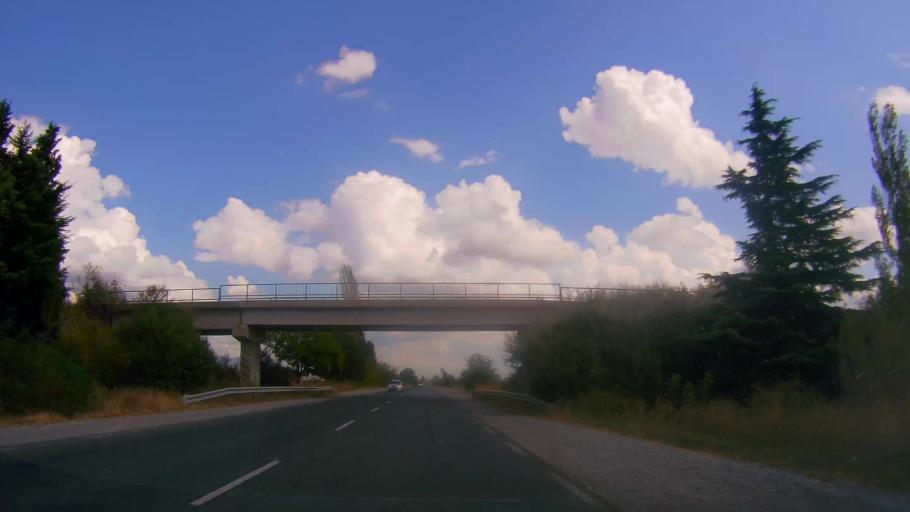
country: BG
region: Sliven
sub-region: Obshtina Sliven
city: Sliven
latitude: 42.6366
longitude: 26.2322
